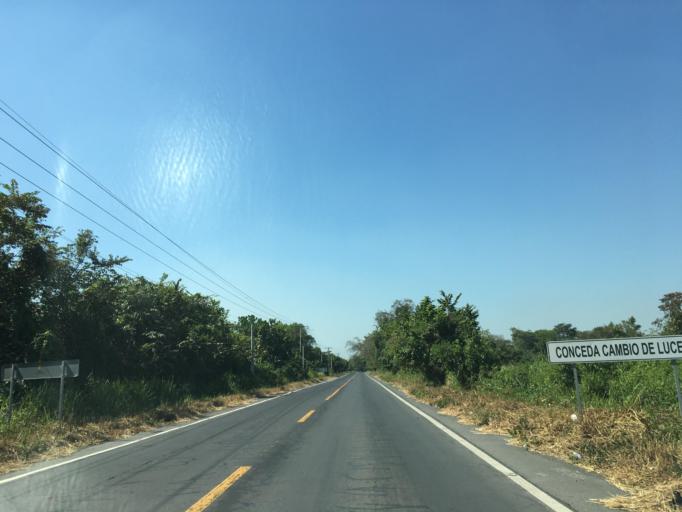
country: GT
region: Escuintla
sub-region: Municipio de Masagua
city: Masagua
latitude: 14.1785
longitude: -90.8683
